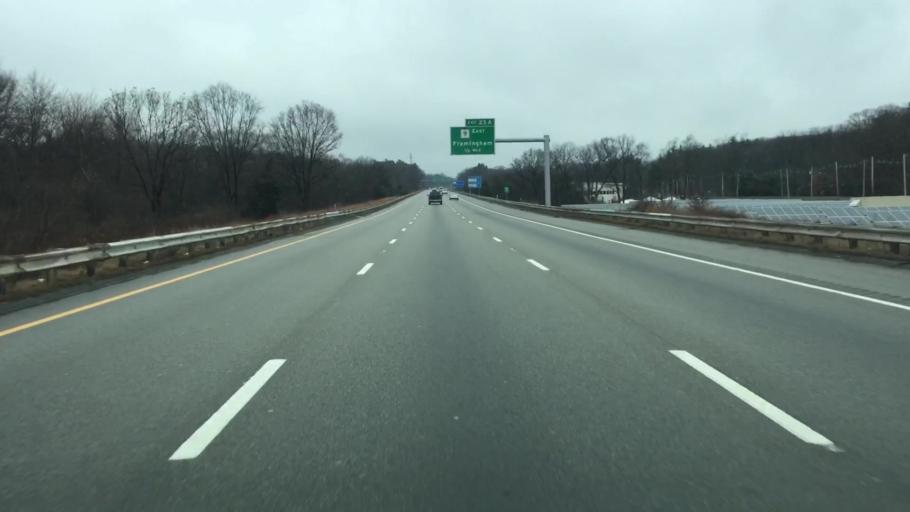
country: US
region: Massachusetts
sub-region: Worcester County
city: Cordaville
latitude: 42.2784
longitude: -71.5657
